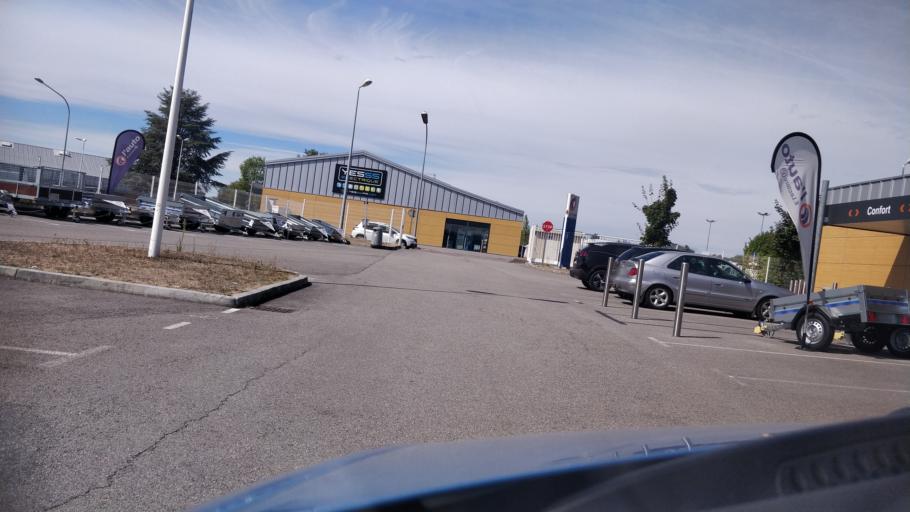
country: FR
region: Limousin
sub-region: Departement de la Haute-Vienne
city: Couzeix
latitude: 45.8710
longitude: 1.2706
